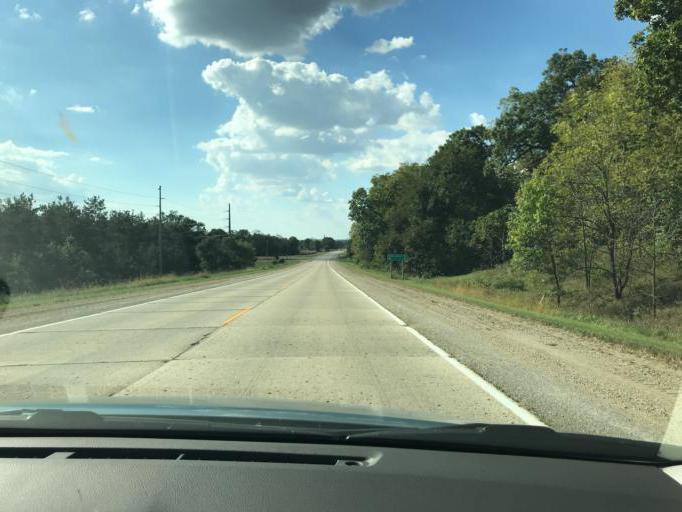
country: US
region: Wisconsin
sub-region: Green County
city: Brodhead
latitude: 42.5632
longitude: -89.3283
